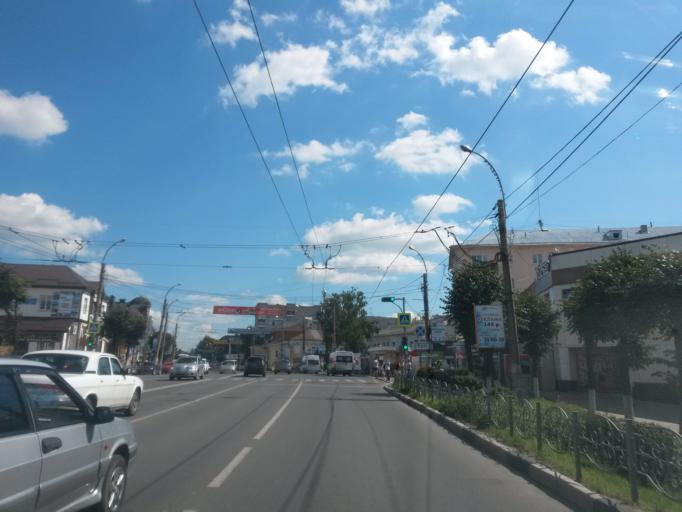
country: RU
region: Ivanovo
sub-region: Gorod Ivanovo
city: Ivanovo
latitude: 56.9955
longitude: 40.9829
